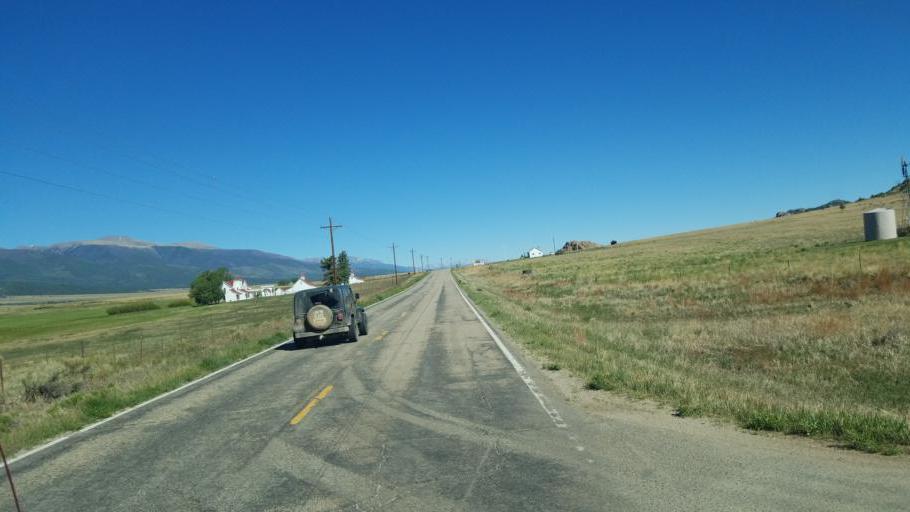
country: US
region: Colorado
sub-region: Custer County
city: Westcliffe
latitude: 38.1904
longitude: -105.5196
